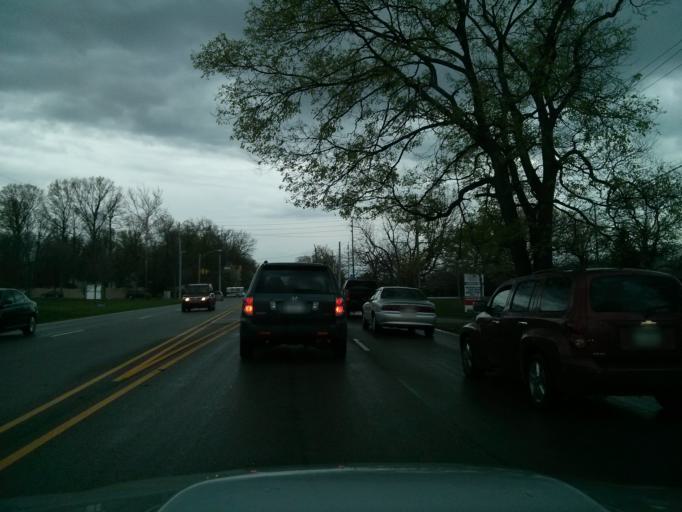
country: US
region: Indiana
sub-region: Marion County
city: Lawrence
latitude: 39.8847
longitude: -86.0462
